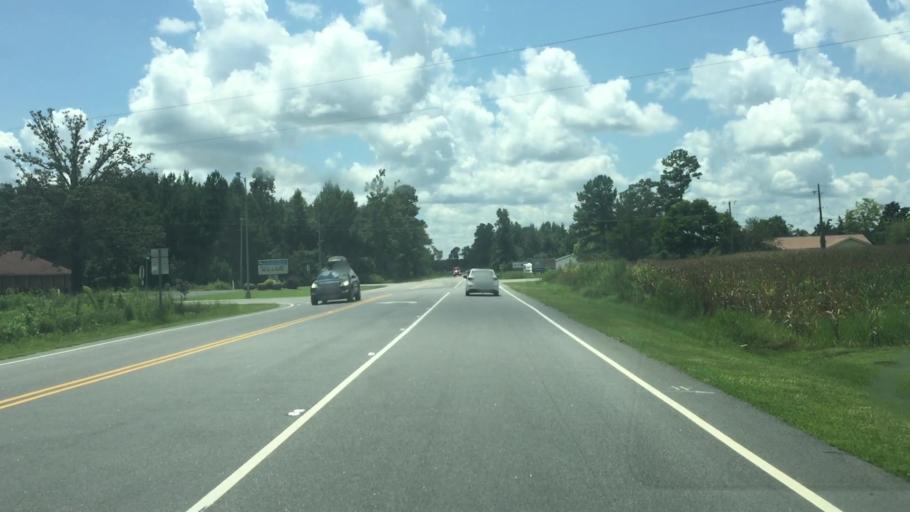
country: US
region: North Carolina
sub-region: Columbus County
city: Tabor City
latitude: 34.2028
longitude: -78.8308
